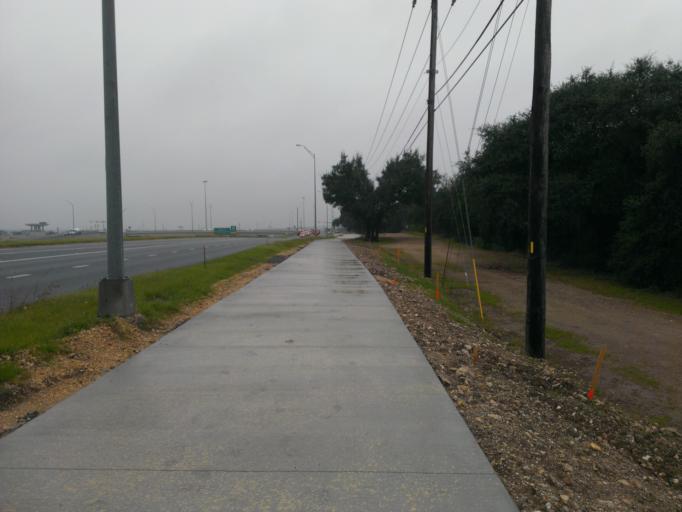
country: US
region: Texas
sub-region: Williamson County
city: Jollyville
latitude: 30.3927
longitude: -97.7345
